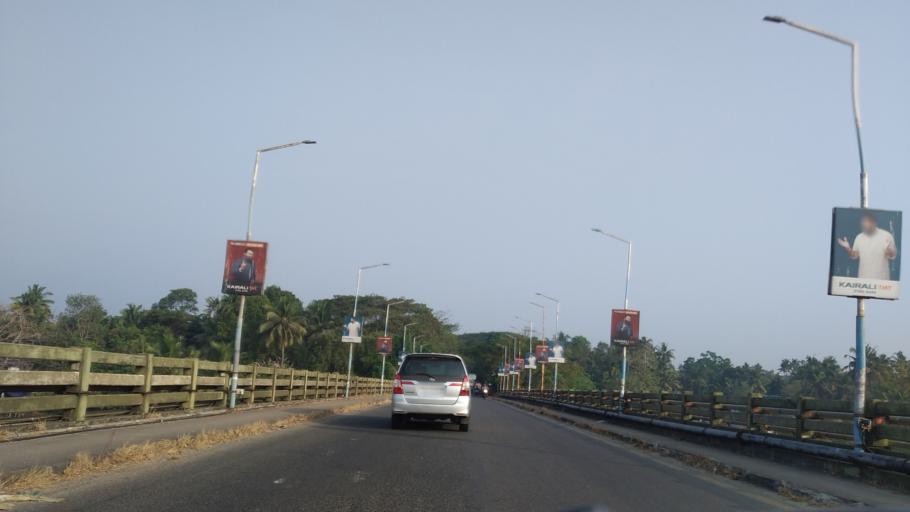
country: IN
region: Kerala
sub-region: Thrissur District
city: Kodungallur
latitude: 10.1997
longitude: 76.2006
